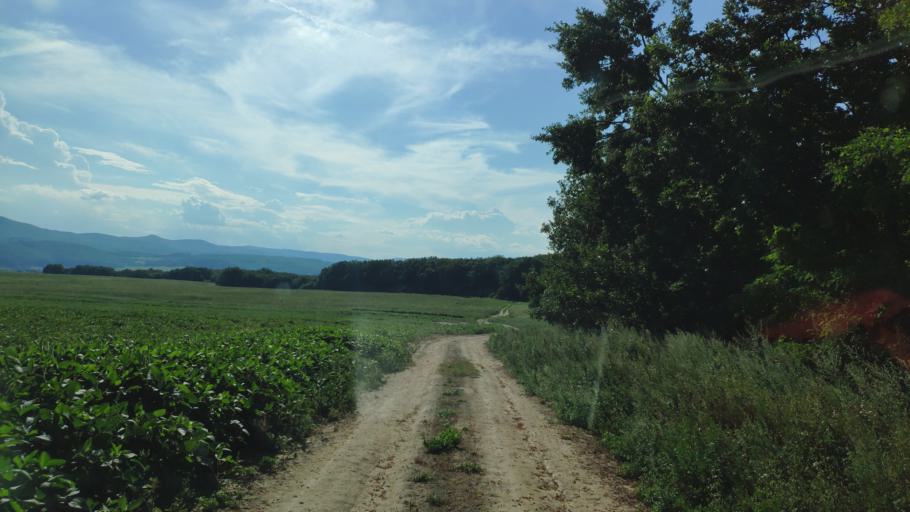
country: SK
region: Presovsky
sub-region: Okres Presov
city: Presov
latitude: 48.9170
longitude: 21.2922
